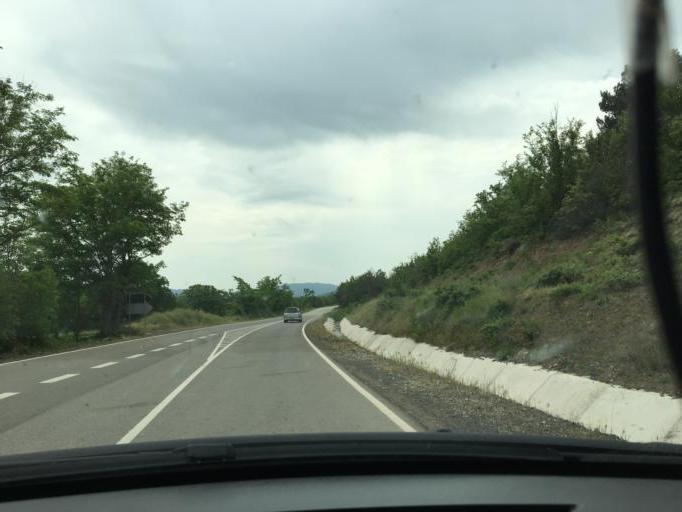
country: MK
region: Gevgelija
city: Miravci
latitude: 41.3038
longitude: 22.4442
